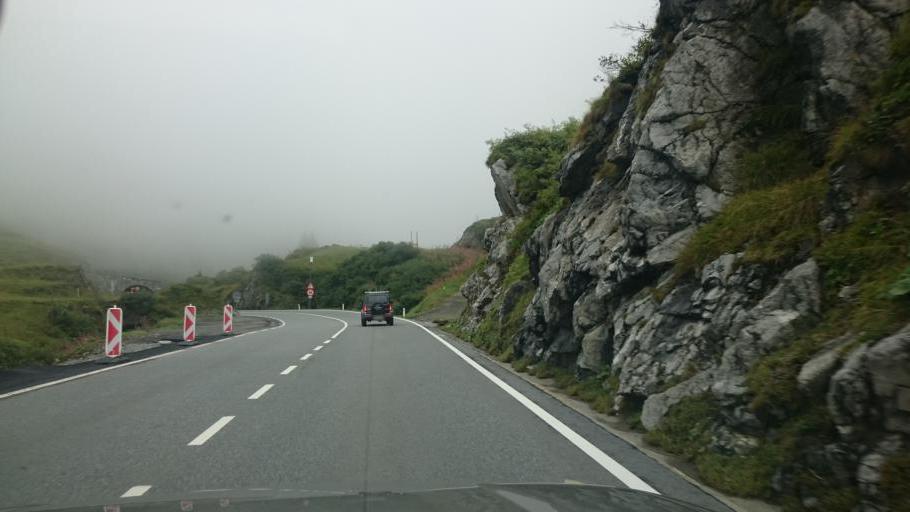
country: AT
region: Vorarlberg
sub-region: Politischer Bezirk Bludenz
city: Lech
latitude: 47.1530
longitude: 10.1650
